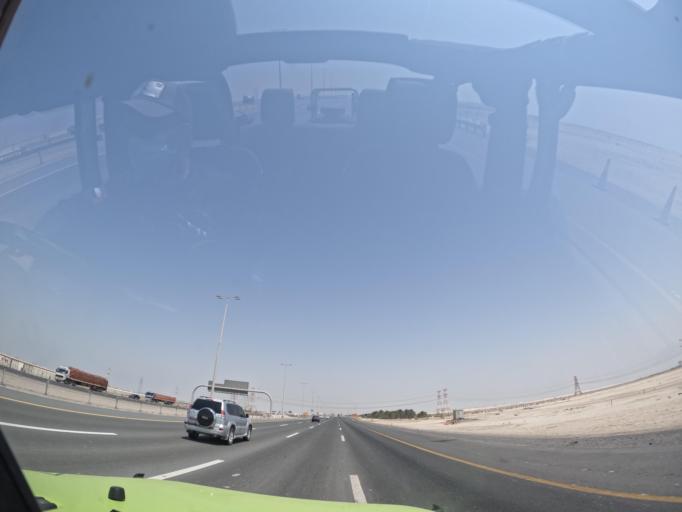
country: AE
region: Abu Dhabi
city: Abu Dhabi
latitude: 24.2170
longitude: 54.4238
